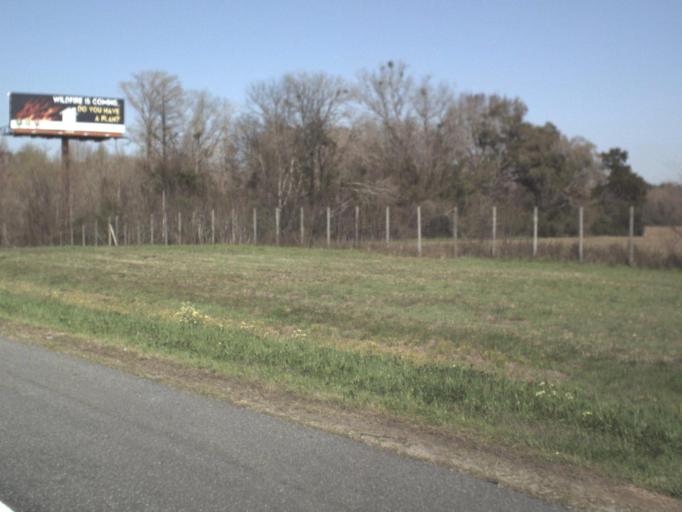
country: US
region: Florida
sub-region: Jackson County
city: Marianna
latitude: 30.7235
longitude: -85.1945
